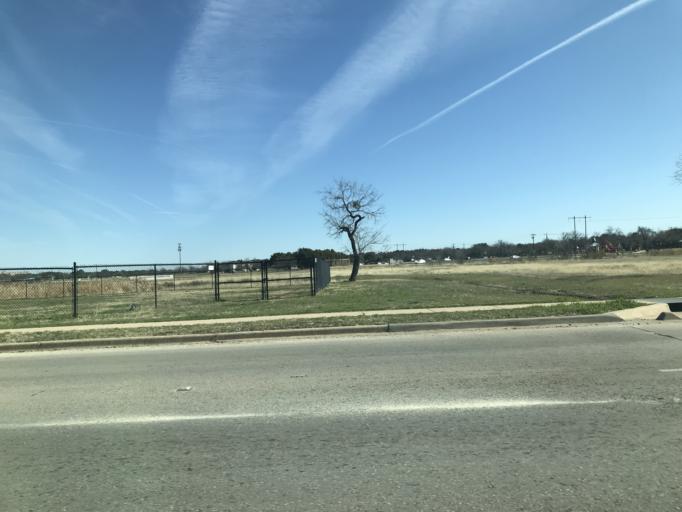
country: US
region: Texas
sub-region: Tom Green County
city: San Angelo
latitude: 31.4314
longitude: -100.4839
